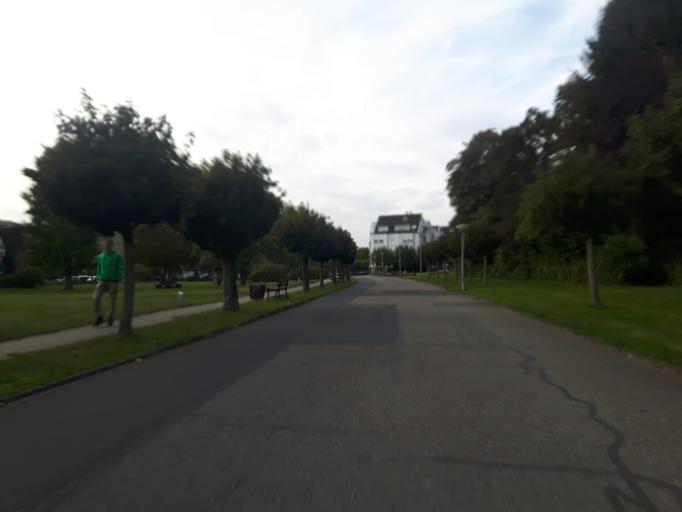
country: DE
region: Rheinland-Pfalz
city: Bad Honningen
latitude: 50.5123
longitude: 7.3091
